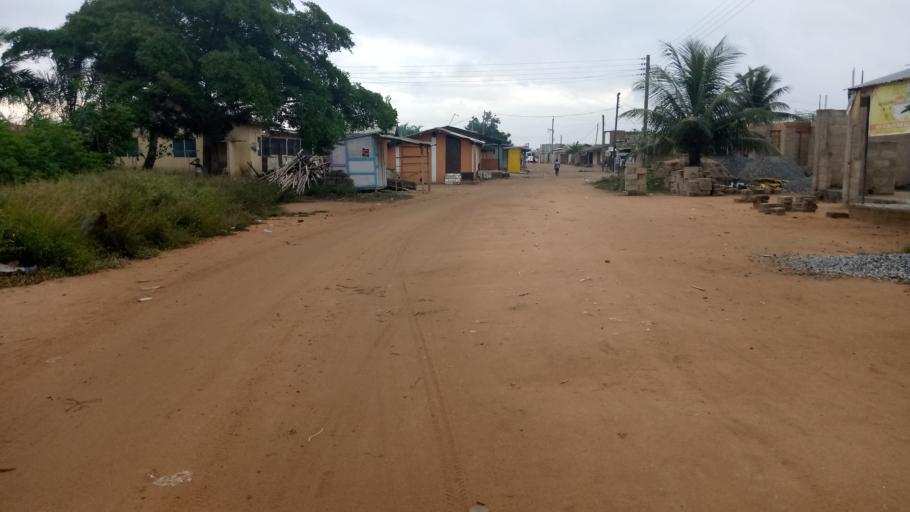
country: GH
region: Central
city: Kasoa
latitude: 5.5015
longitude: -0.4103
